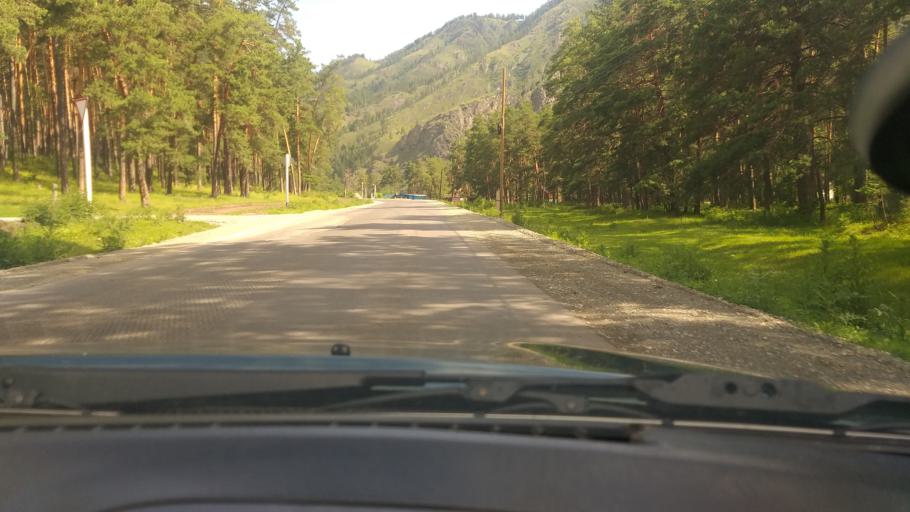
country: RU
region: Altay
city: Chemal
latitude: 51.3955
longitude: 86.0228
